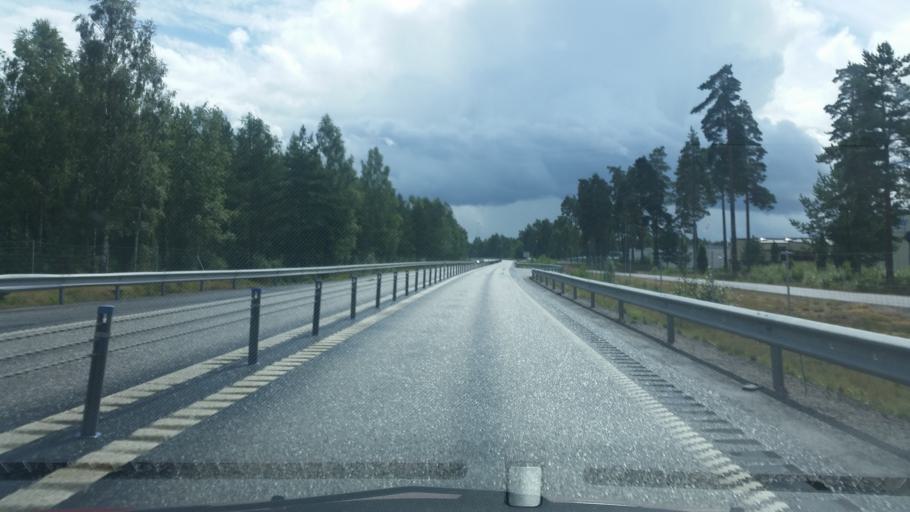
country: SE
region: Joenkoeping
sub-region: Gislaveds Kommun
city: Gislaved
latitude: 57.2773
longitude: 13.6145
